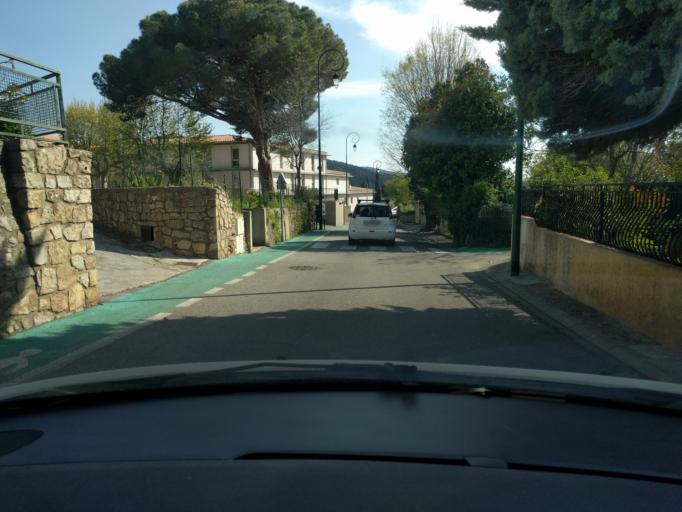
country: FR
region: Provence-Alpes-Cote d'Azur
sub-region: Departement du Var
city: Pierrefeu-du-Var
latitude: 43.2244
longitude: 6.1439
